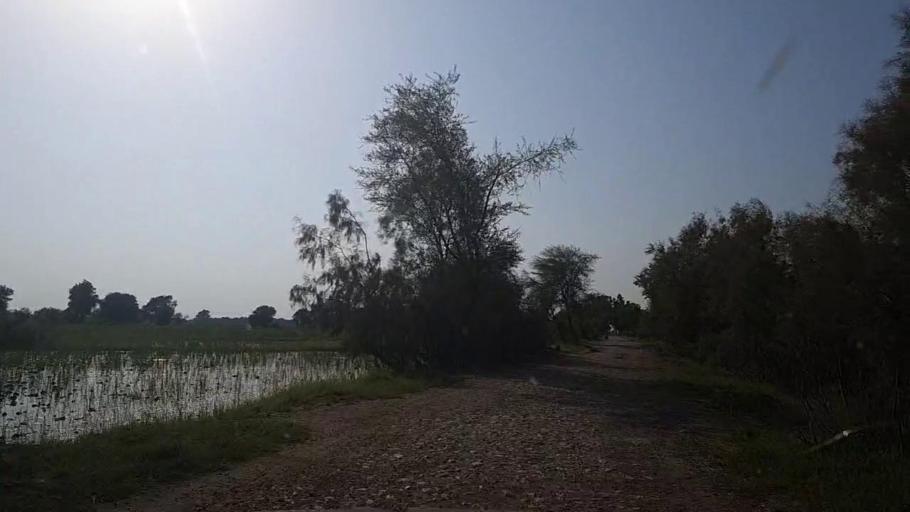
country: PK
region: Sindh
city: Khanpur
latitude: 27.7052
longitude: 69.3348
